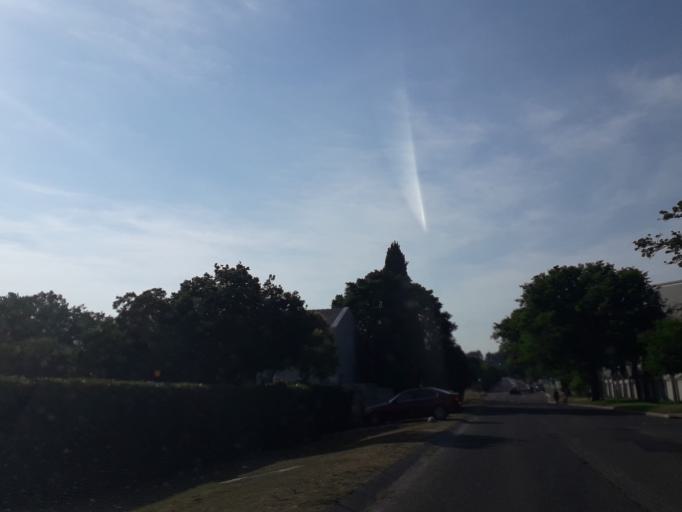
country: ZA
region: Gauteng
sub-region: City of Johannesburg Metropolitan Municipality
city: Diepsloot
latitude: -26.0306
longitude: 28.0146
